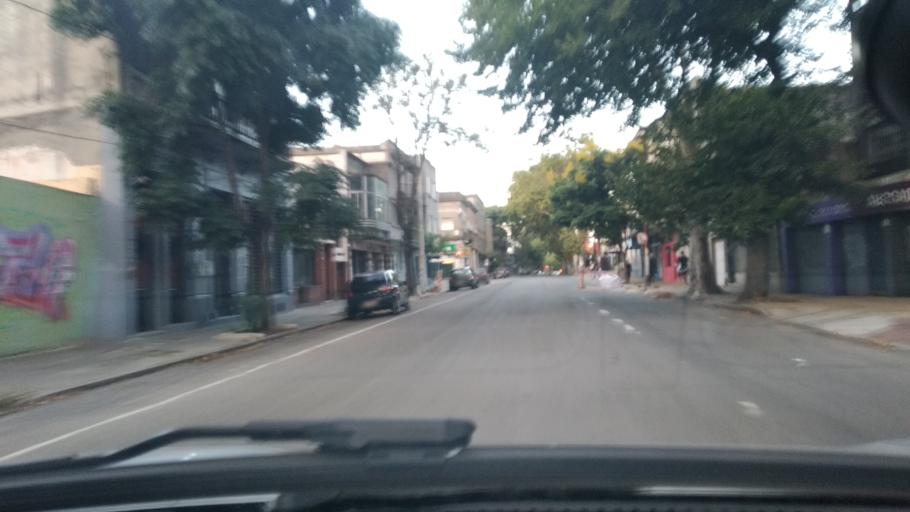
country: UY
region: Montevideo
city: Montevideo
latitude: -34.8993
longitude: -56.1744
